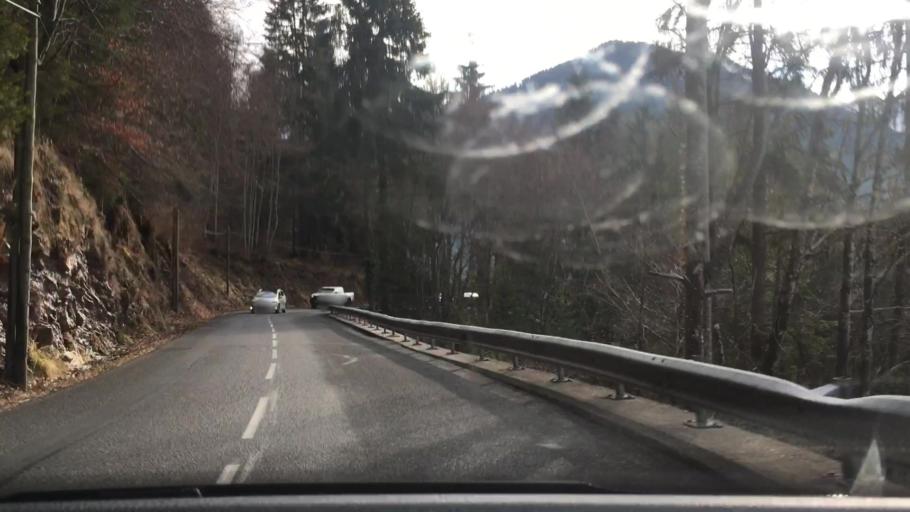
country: FR
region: Rhone-Alpes
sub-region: Departement de la Haute-Savoie
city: Abondance
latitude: 46.2702
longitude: 6.6317
